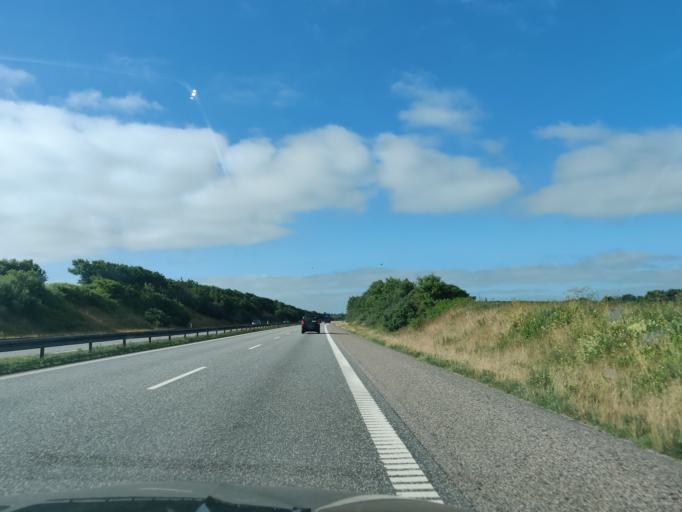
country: DK
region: North Denmark
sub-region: Rebild Kommune
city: Stovring
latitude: 56.8055
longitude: 9.7122
